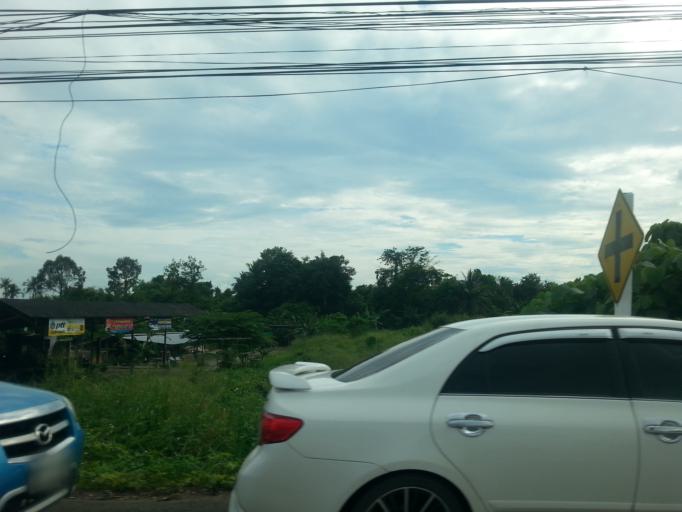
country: TH
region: Krabi
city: Krabi
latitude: 8.1034
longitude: 98.8978
